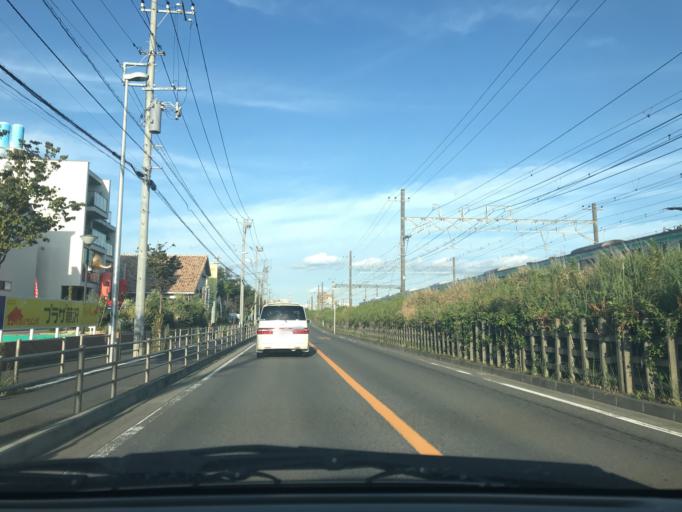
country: JP
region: Kanagawa
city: Fujisawa
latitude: 35.3380
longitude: 139.4666
